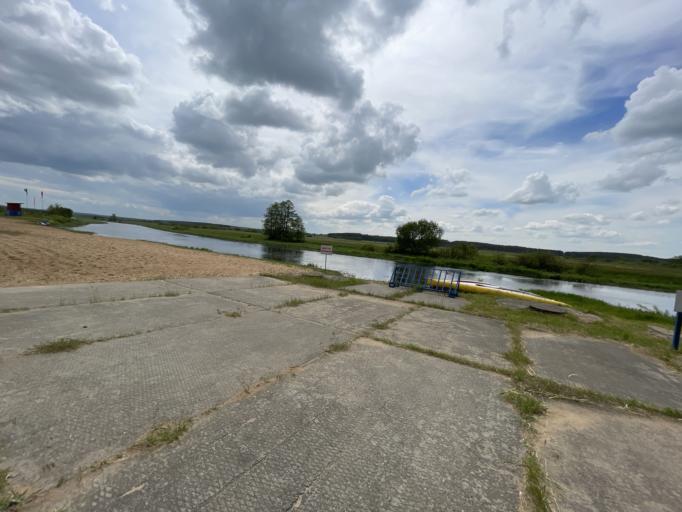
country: BY
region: Minsk
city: Stowbtsy
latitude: 53.4246
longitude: 26.8153
